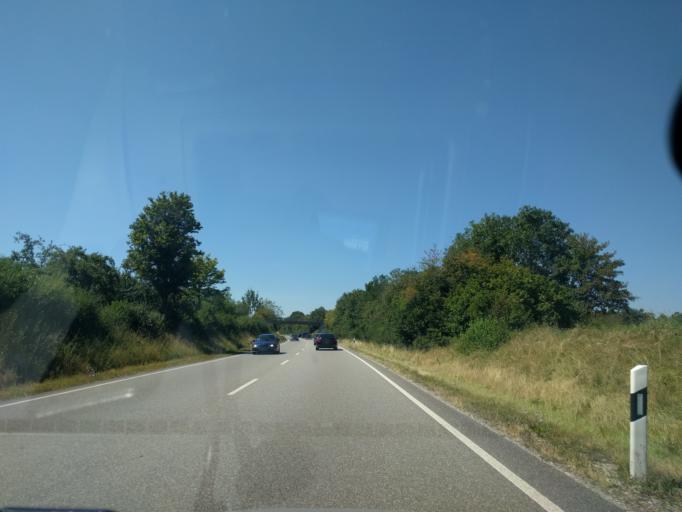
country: DE
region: Bavaria
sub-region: Upper Bavaria
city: Emmering
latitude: 48.1931
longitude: 11.2810
